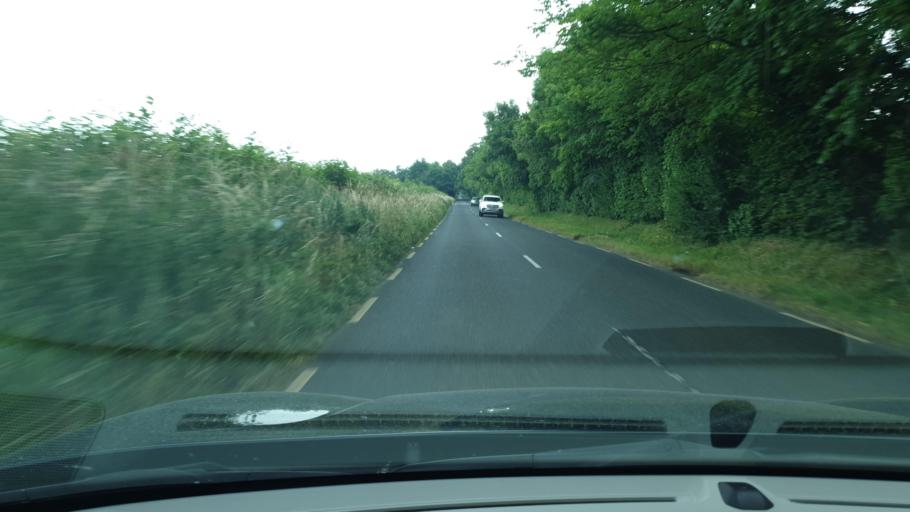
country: IE
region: Leinster
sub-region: An Mhi
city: Ratoath
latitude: 53.5183
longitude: -6.4730
